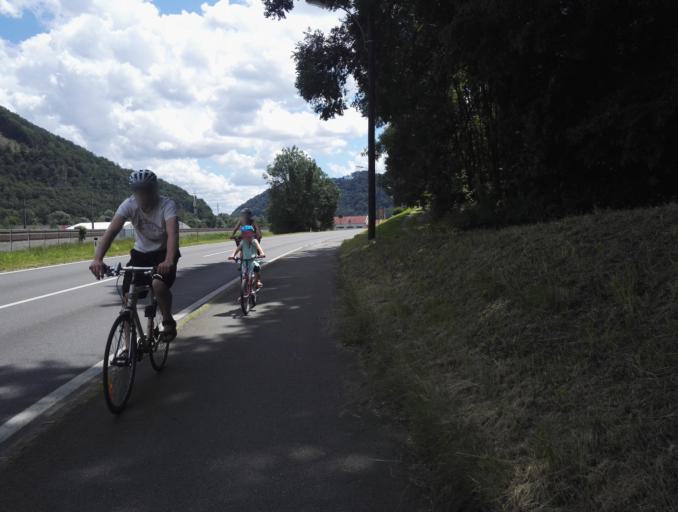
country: AT
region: Styria
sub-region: Politischer Bezirk Graz-Umgebung
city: Gratkorn
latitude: 47.1176
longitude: 15.3680
